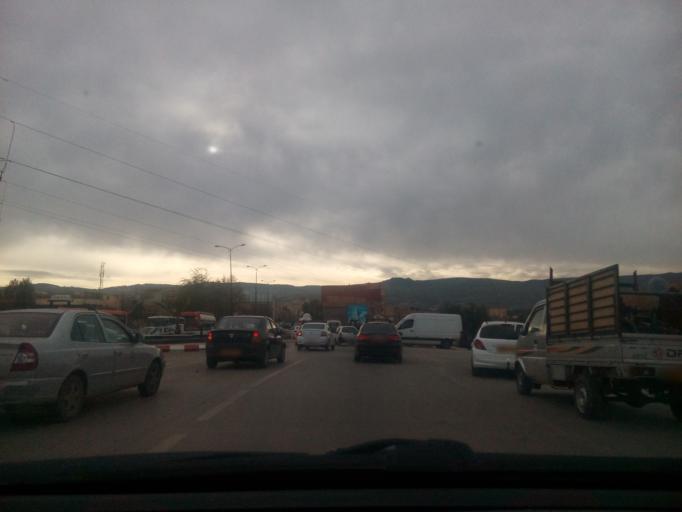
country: DZ
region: Tlemcen
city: Mansoura
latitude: 34.8849
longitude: -1.3523
